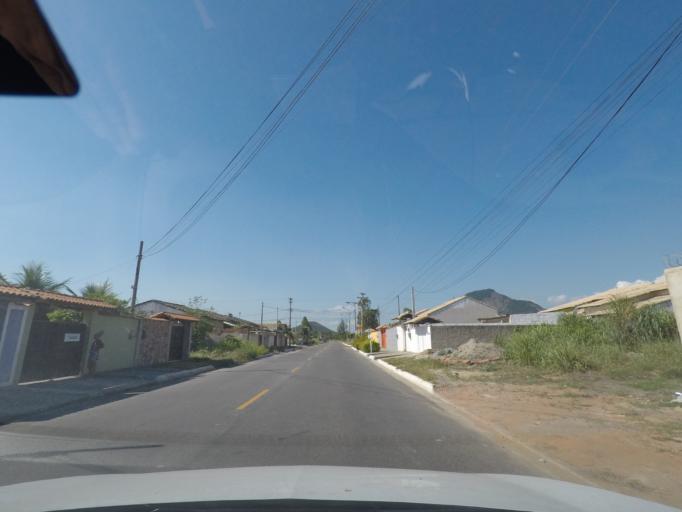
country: BR
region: Rio de Janeiro
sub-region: Marica
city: Marica
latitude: -22.9600
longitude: -42.9272
